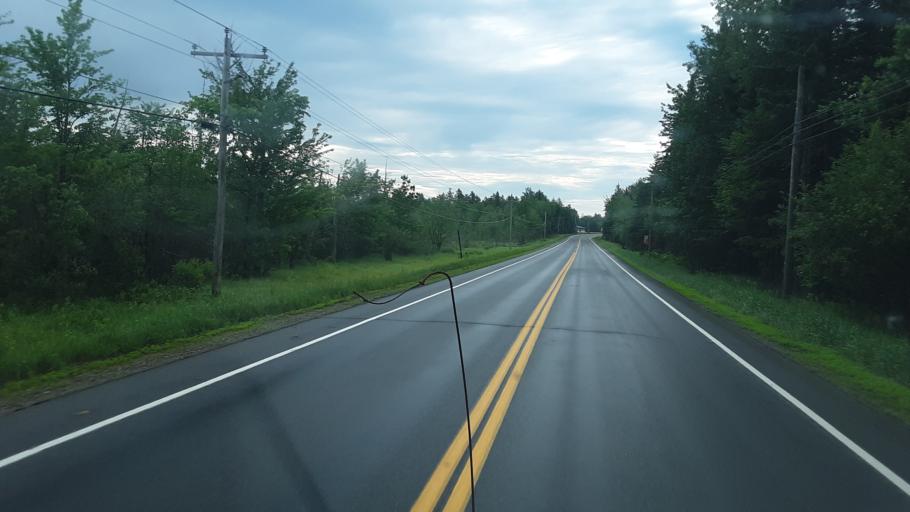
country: US
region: Maine
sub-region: Penobscot County
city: Patten
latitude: 45.9281
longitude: -68.4441
